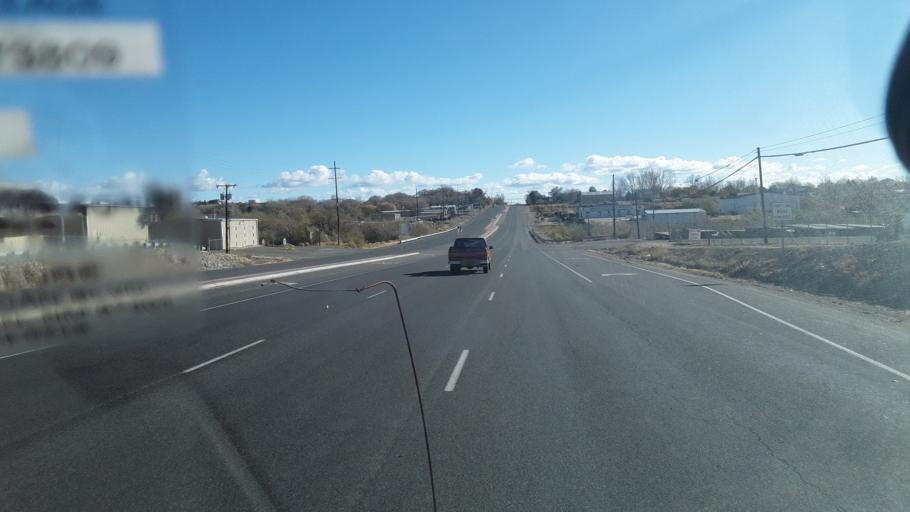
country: US
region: New Mexico
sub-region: San Juan County
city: Lee Acres
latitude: 36.7010
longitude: -108.0662
